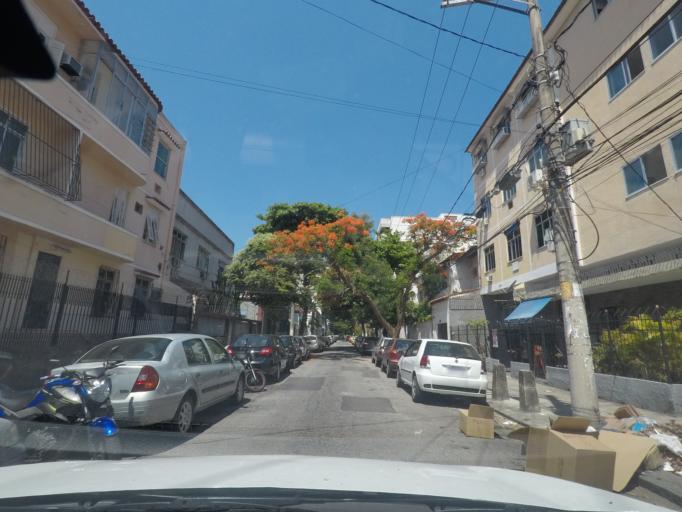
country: BR
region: Rio de Janeiro
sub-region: Rio De Janeiro
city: Rio de Janeiro
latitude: -22.9193
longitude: -43.2404
